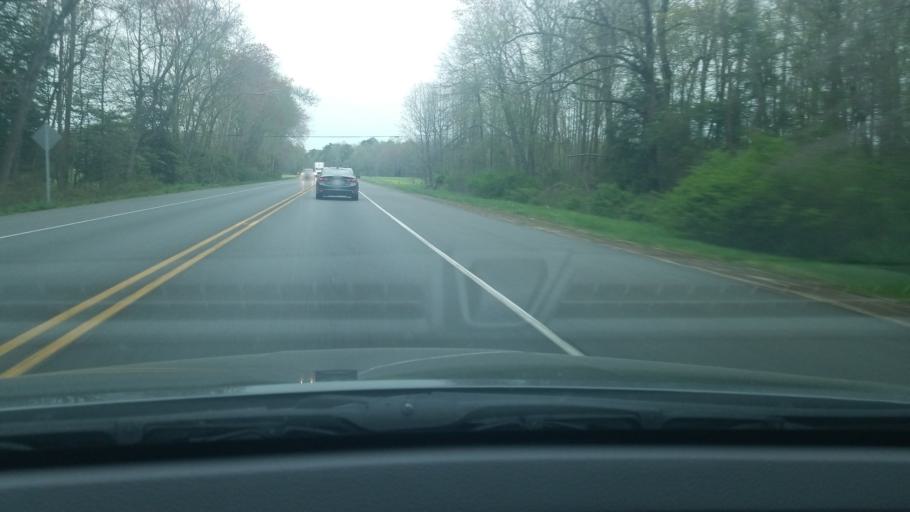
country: US
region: New Jersey
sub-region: Burlington County
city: Leisuretowne
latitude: 39.8867
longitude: -74.7367
